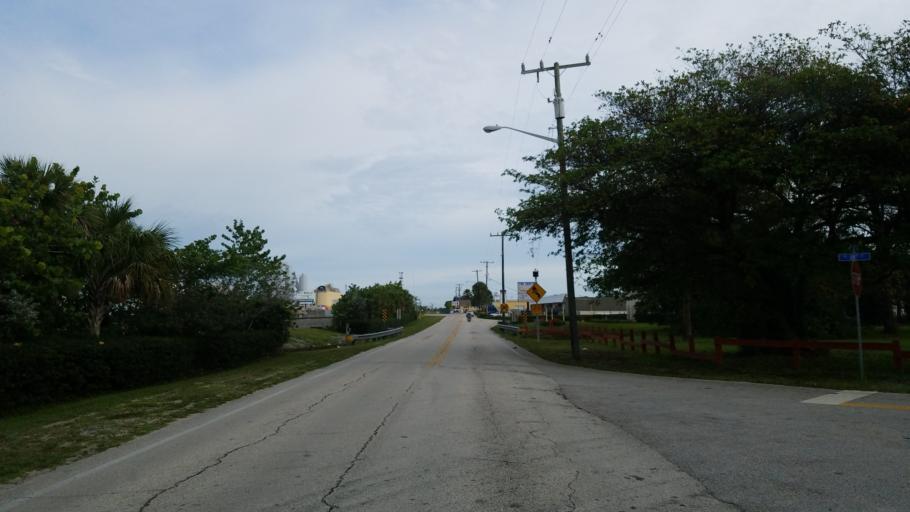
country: US
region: Florida
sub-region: Martin County
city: Stuart
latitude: 27.1865
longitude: -80.2415
